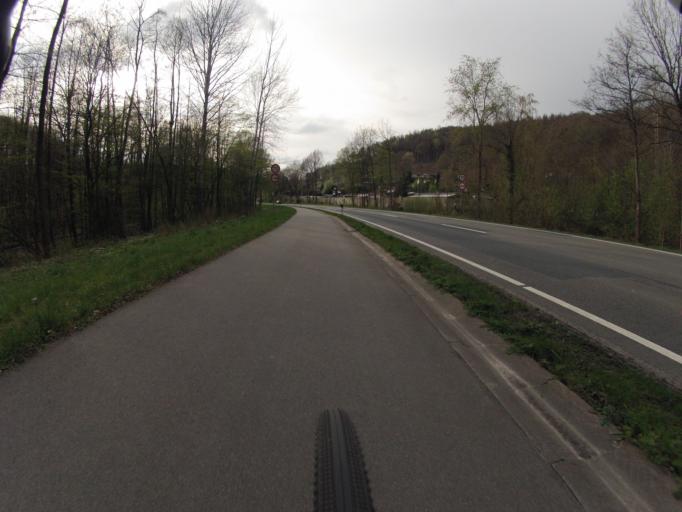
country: DE
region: North Rhine-Westphalia
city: Ibbenburen
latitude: 52.2339
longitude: 7.7490
